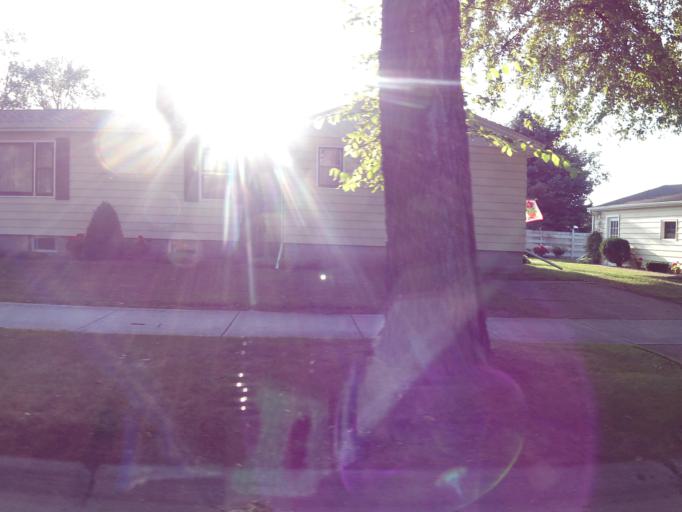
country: US
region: North Dakota
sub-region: Grand Forks County
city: Grand Forks
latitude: 47.8991
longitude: -97.0406
